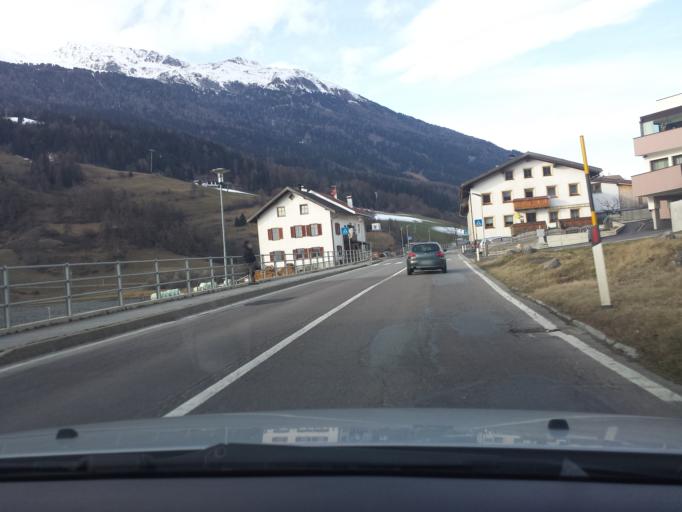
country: IT
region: Trentino-Alto Adige
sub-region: Bolzano
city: Curon Venosta
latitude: 46.7604
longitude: 10.5356
